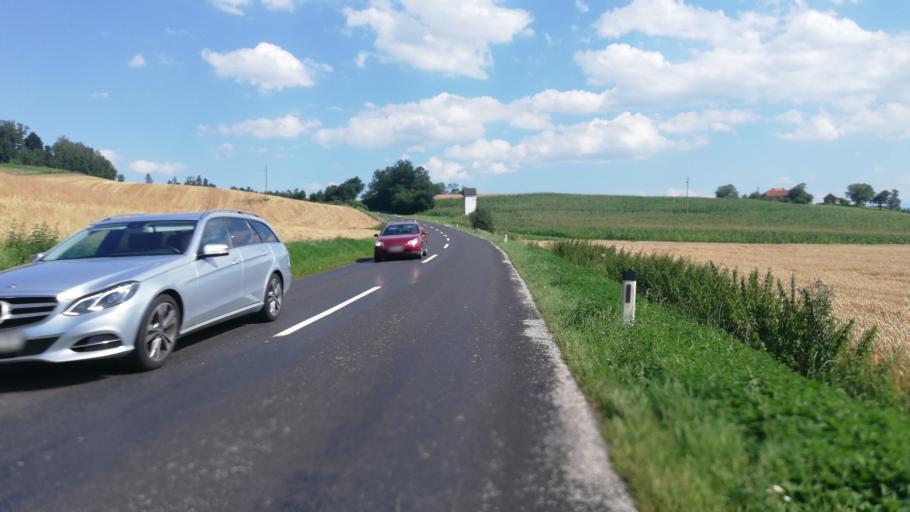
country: AT
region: Upper Austria
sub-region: Wels-Land
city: Gunskirchen
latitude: 48.1598
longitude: 13.9197
